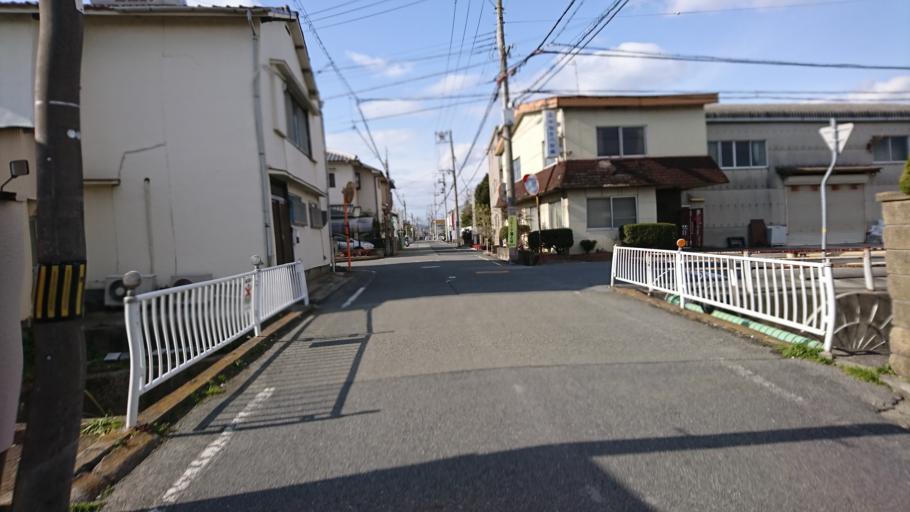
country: JP
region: Hyogo
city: Kakogawacho-honmachi
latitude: 34.7597
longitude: 134.8326
